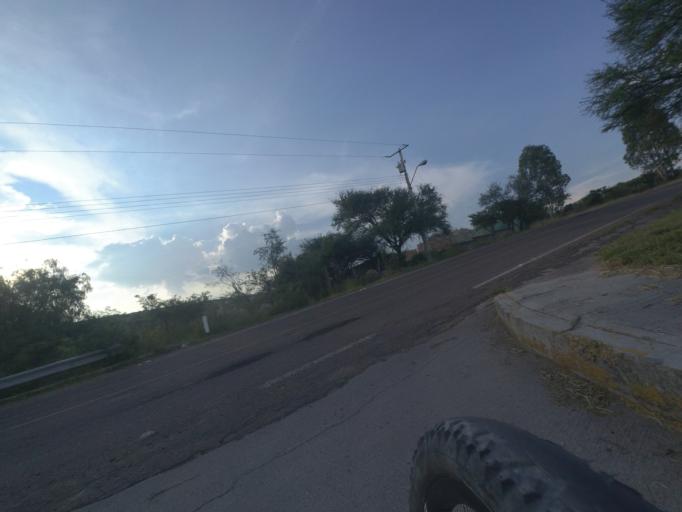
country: MX
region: Aguascalientes
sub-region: Aguascalientes
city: Los Canos
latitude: 21.7806
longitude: -102.3777
